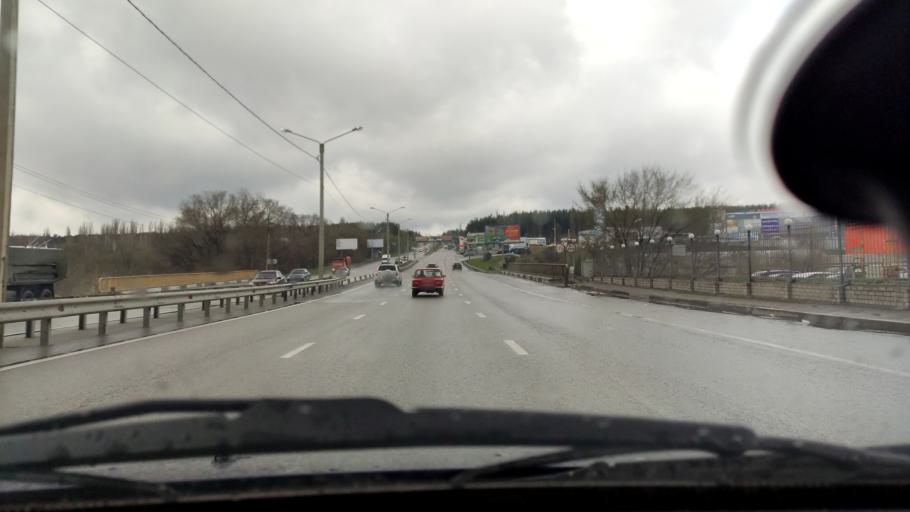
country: RU
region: Voronezj
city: Pridonskoy
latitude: 51.6680
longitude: 39.1234
